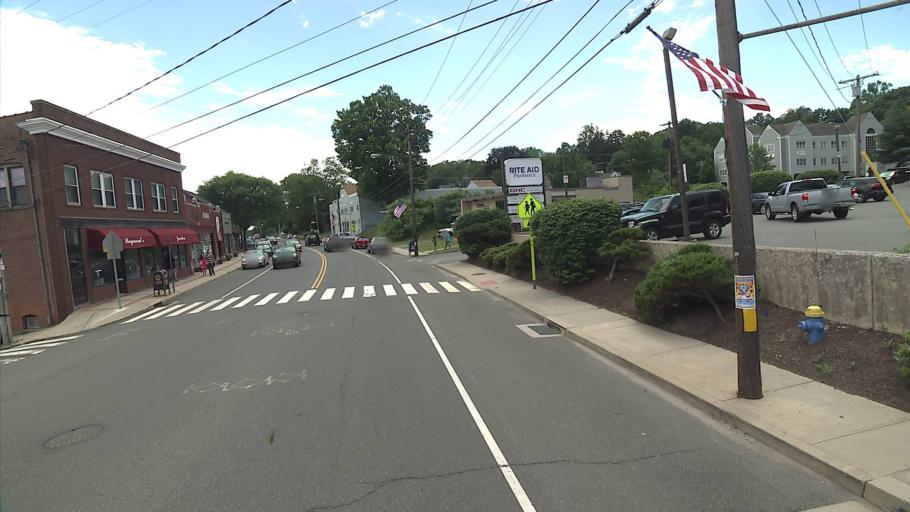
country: US
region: Connecticut
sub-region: Litchfield County
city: Watertown
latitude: 41.6019
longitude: -73.1161
